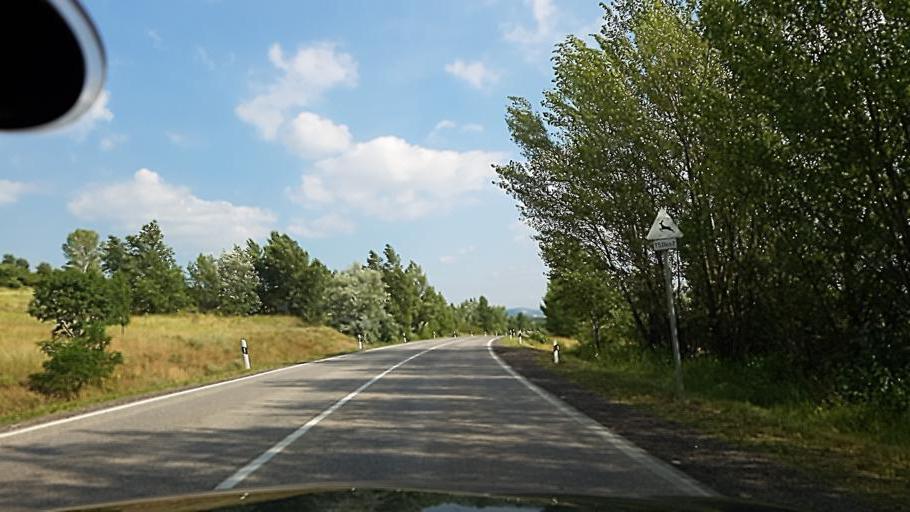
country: HU
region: Komarom-Esztergom
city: Dorog
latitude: 47.7341
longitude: 18.7563
